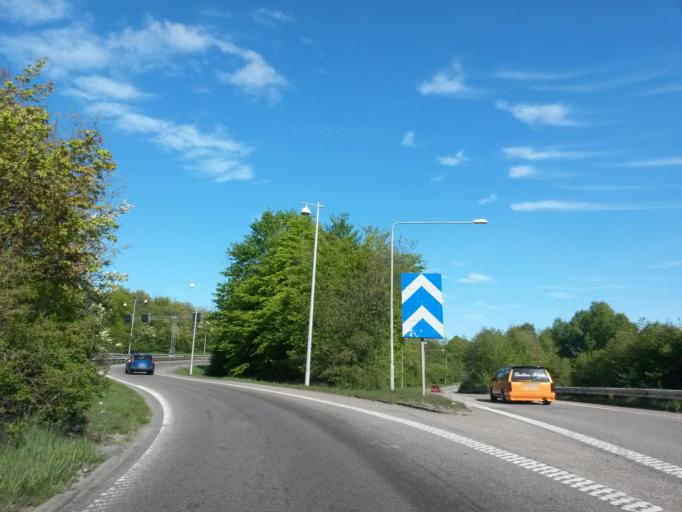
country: SE
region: Vaestra Goetaland
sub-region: Goteborg
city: Goeteborg
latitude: 57.7260
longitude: 11.9714
